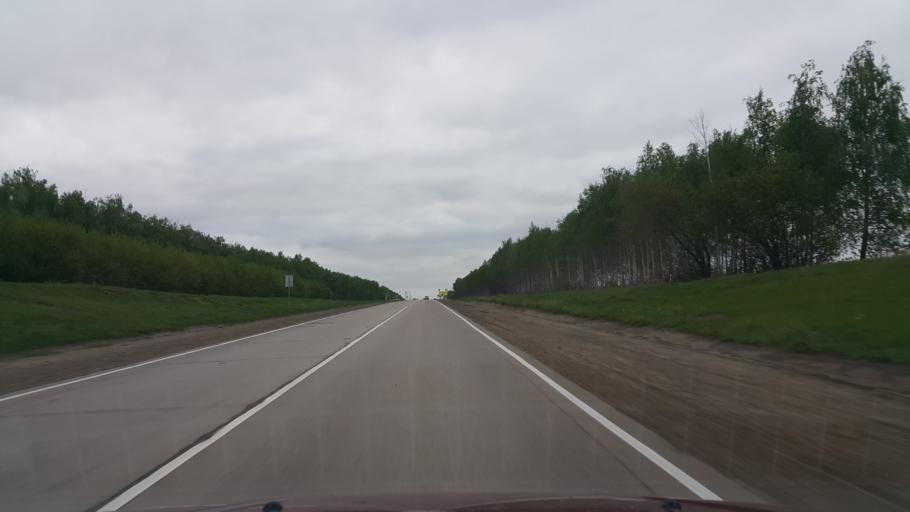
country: RU
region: Tambov
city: Znamenka
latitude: 52.3974
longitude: 41.3957
